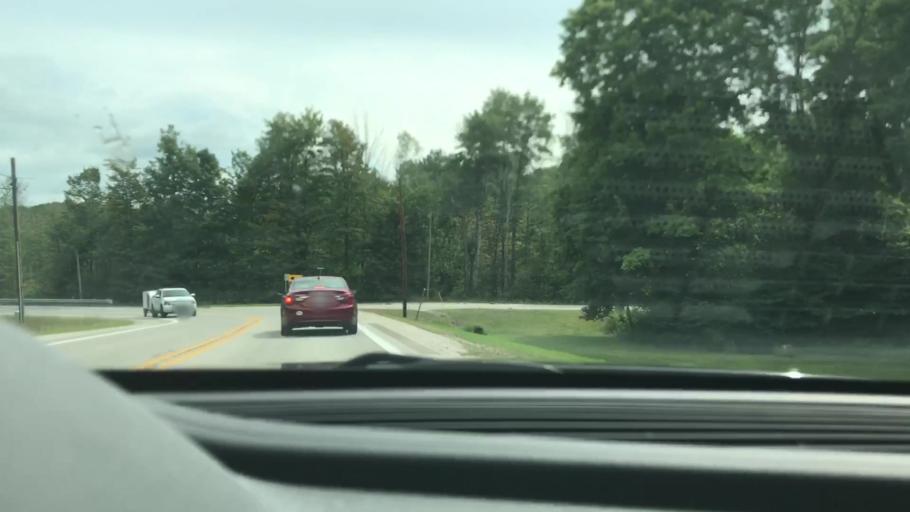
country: US
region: Michigan
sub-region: Antrim County
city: Bellaire
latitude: 45.0796
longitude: -85.2830
